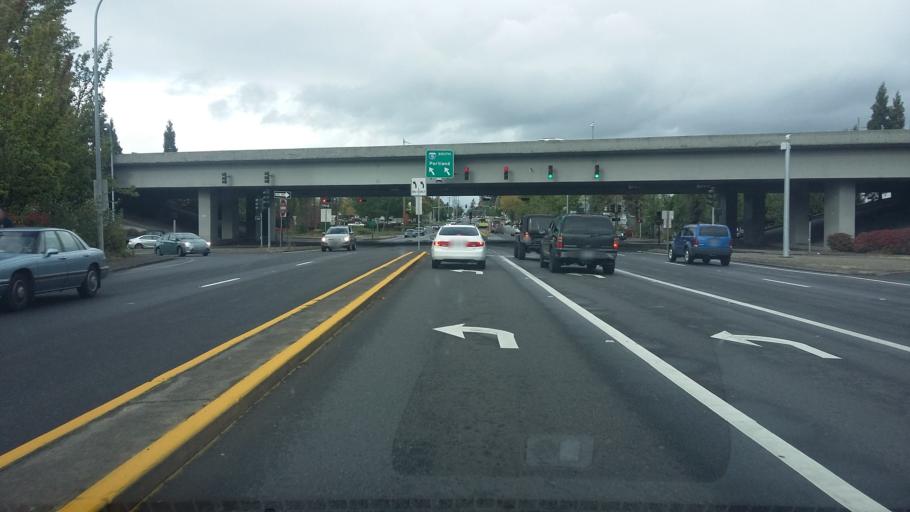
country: US
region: Washington
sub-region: Clark County
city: Salmon Creek
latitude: 45.6930
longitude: -122.6601
